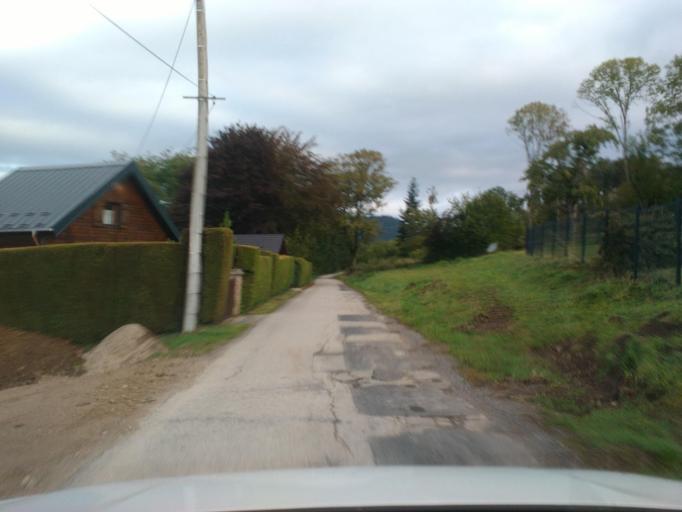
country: FR
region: Lorraine
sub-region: Departement des Vosges
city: Senones
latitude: 48.3930
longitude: 7.0383
